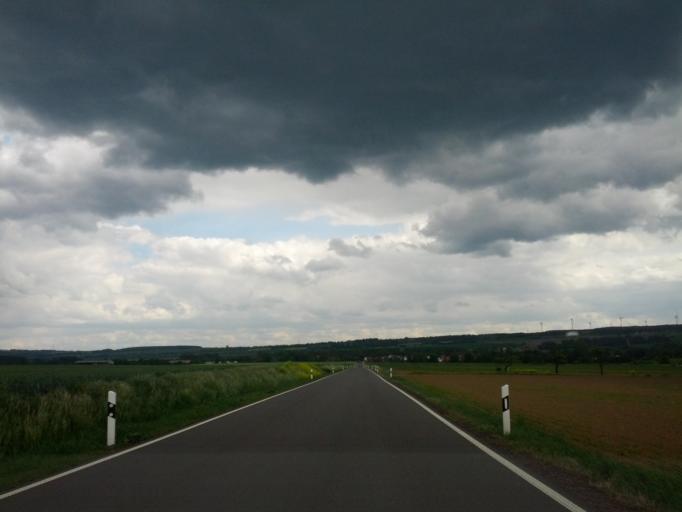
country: DE
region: Thuringia
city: Friedrichswerth
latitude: 51.0057
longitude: 10.5392
